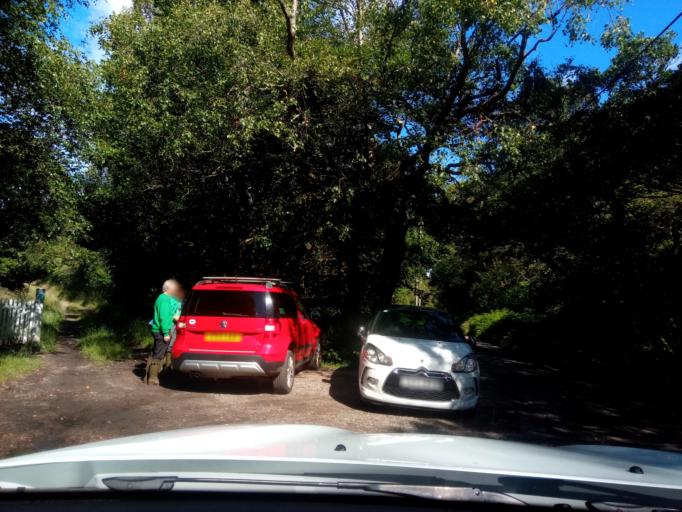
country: GB
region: Scotland
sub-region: Argyll and Bute
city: Isle Of Mull
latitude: 56.7652
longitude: -5.8209
